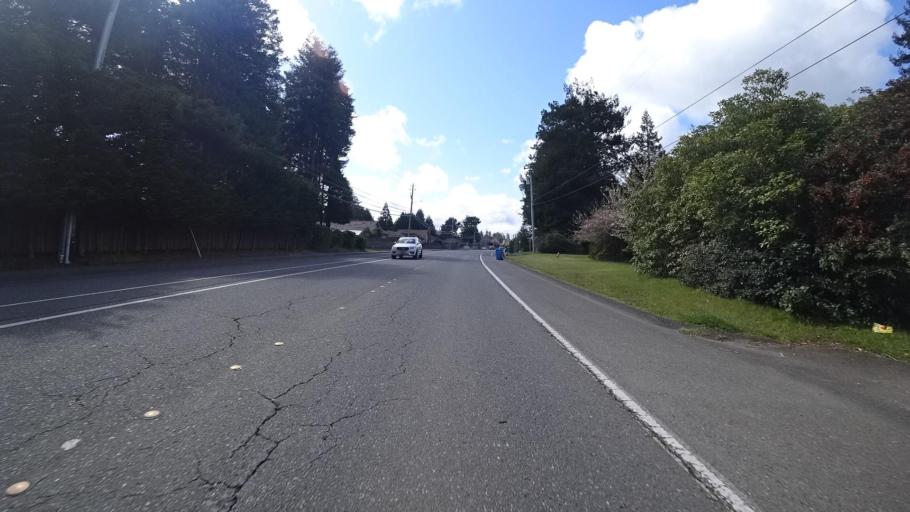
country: US
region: California
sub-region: Humboldt County
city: Pine Hills
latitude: 40.7448
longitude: -124.1475
